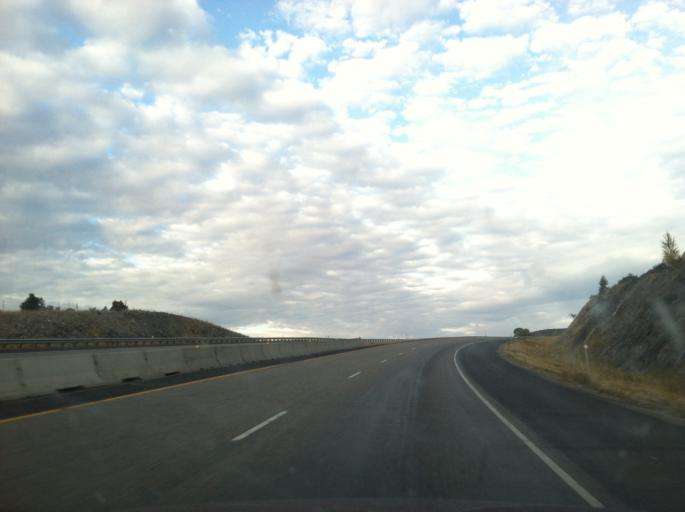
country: US
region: Montana
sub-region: Jefferson County
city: Whitehall
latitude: 45.8782
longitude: -111.8831
